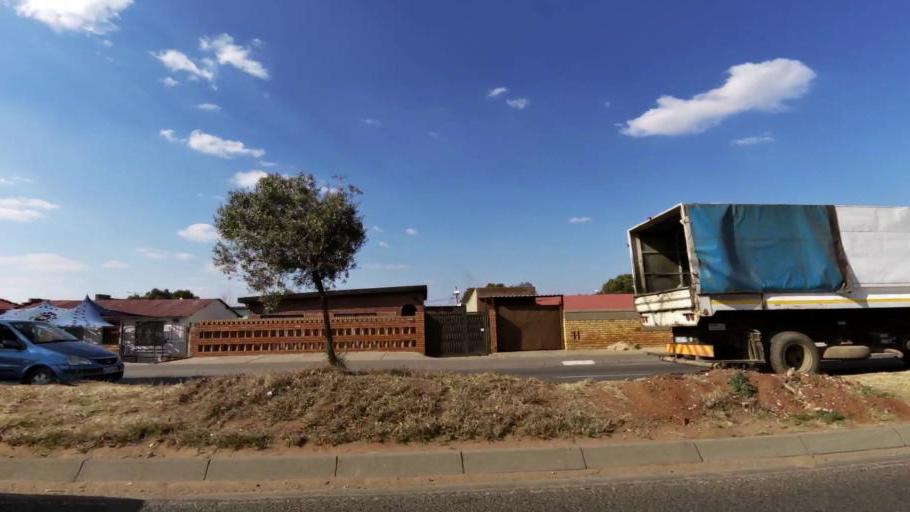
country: ZA
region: Gauteng
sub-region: City of Johannesburg Metropolitan Municipality
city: Soweto
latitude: -26.2196
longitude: 27.8718
